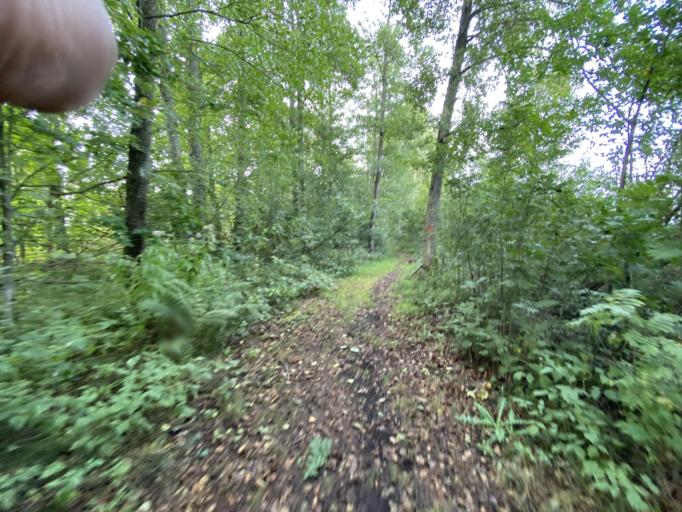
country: SE
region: Skane
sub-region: Hassleholms Kommun
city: Hastveda
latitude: 56.3630
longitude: 13.8831
